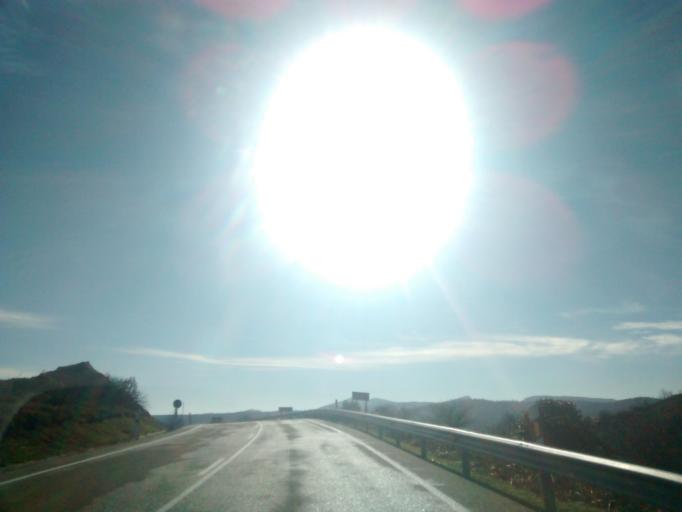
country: ES
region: Castille and Leon
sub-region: Provincia de Burgos
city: Arija
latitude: 42.9899
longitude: -3.8202
